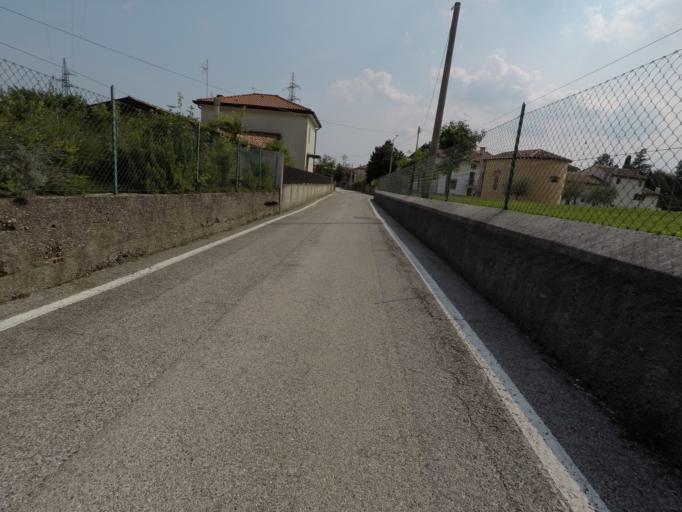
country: IT
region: Friuli Venezia Giulia
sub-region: Provincia di Pordenone
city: Caneva
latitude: 45.9681
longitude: 12.4398
